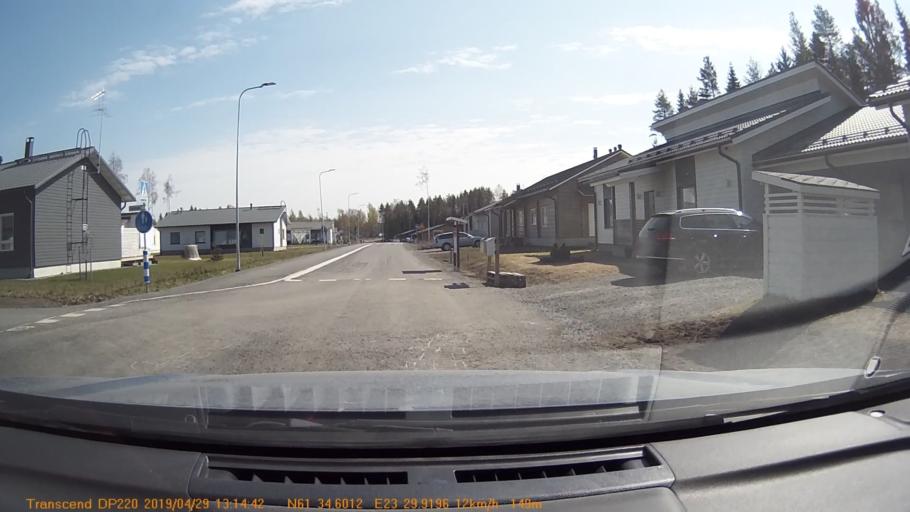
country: FI
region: Pirkanmaa
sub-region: Tampere
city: Yloejaervi
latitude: 61.5768
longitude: 23.4992
